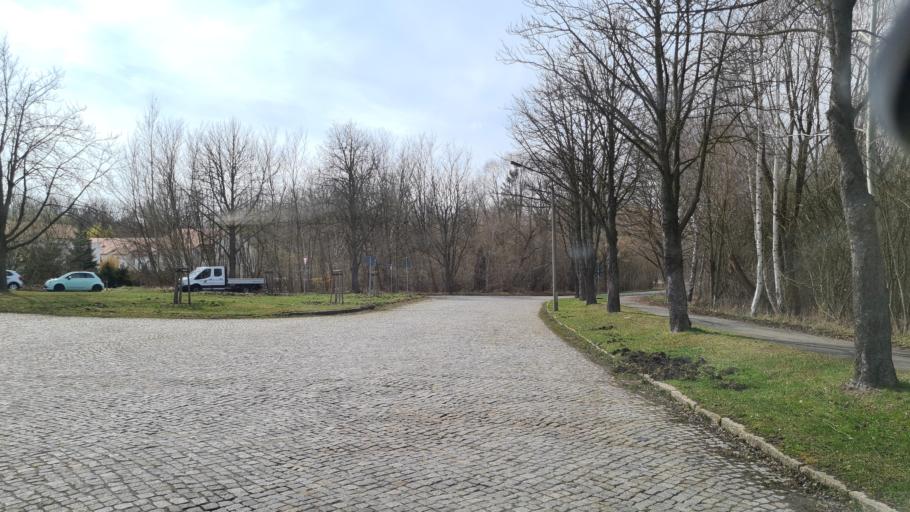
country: DE
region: Brandenburg
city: Lauchhammer
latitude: 51.4954
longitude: 13.7429
